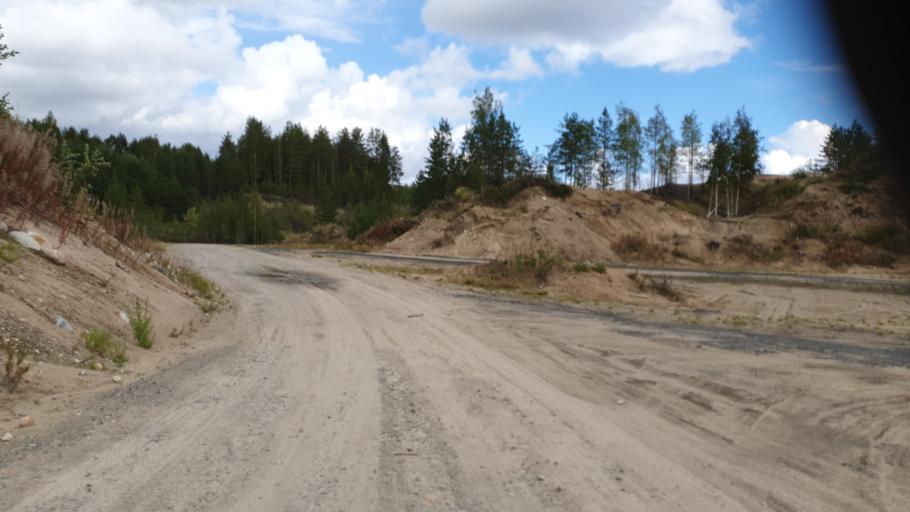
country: FI
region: Kainuu
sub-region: Kehys-Kainuu
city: Kuhmo
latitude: 64.1514
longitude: 29.3711
